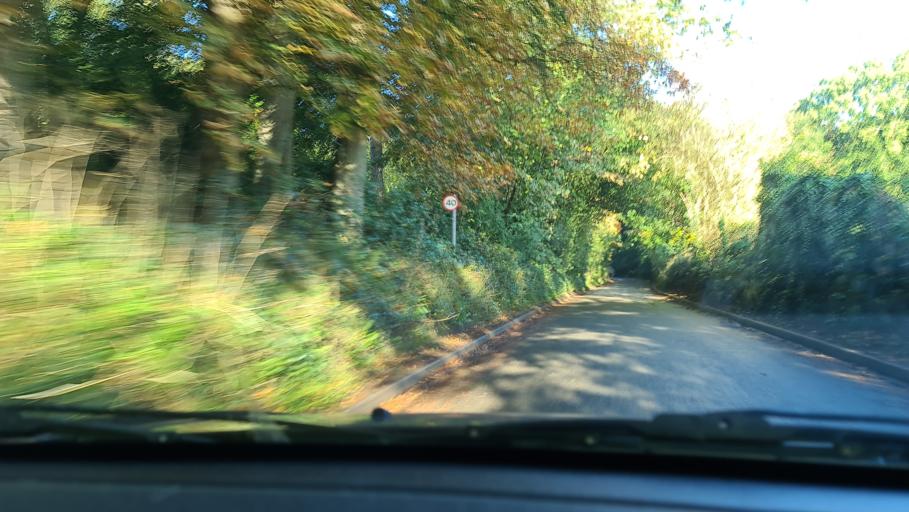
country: GB
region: England
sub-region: Hertfordshire
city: Chorleywood
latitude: 51.6386
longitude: -0.5147
